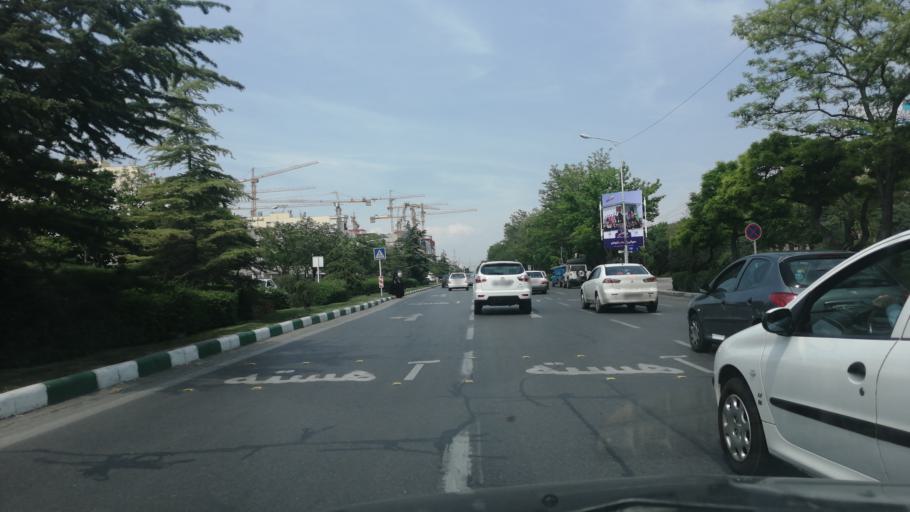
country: IR
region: Razavi Khorasan
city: Mashhad
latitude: 36.3124
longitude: 59.5577
